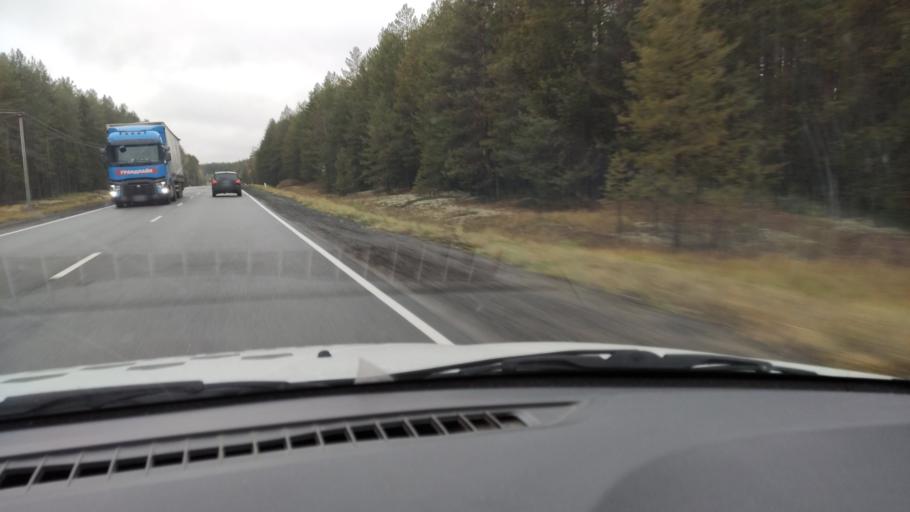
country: RU
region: Kirov
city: Belaya Kholunitsa
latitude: 58.9080
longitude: 50.9980
